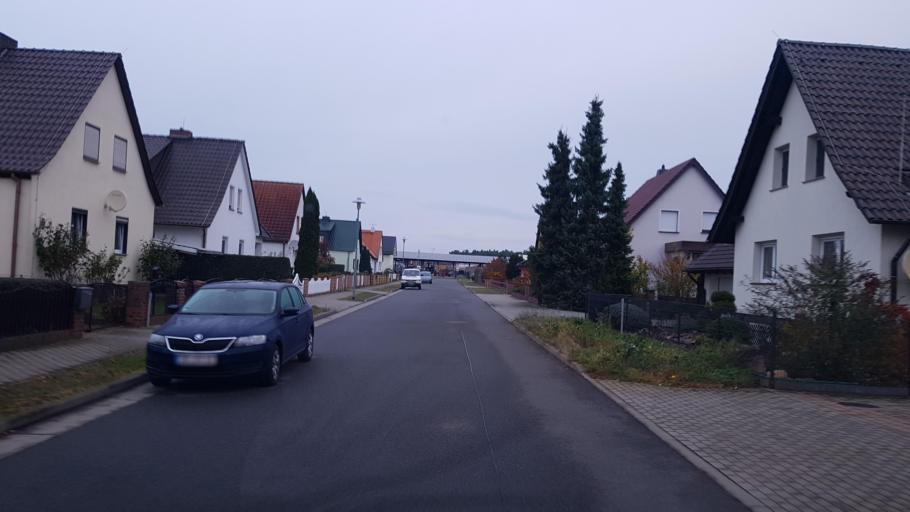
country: DE
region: Saxony-Anhalt
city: Jessen
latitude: 51.7962
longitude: 12.9527
